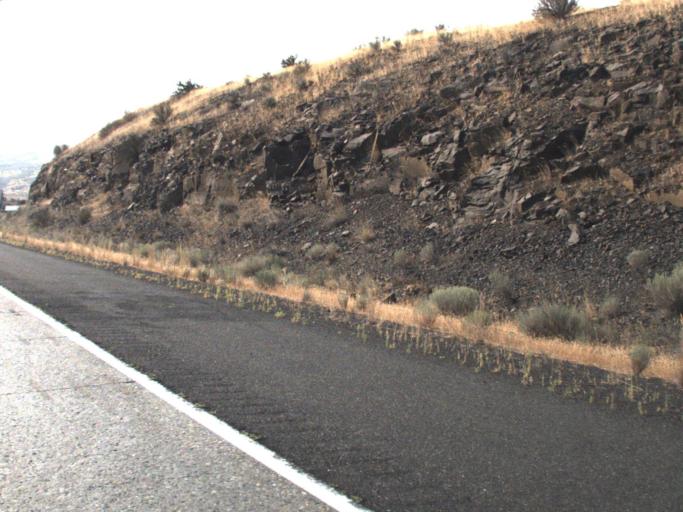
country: US
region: Washington
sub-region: Kittitas County
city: Kittitas
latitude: 46.8160
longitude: -120.3552
